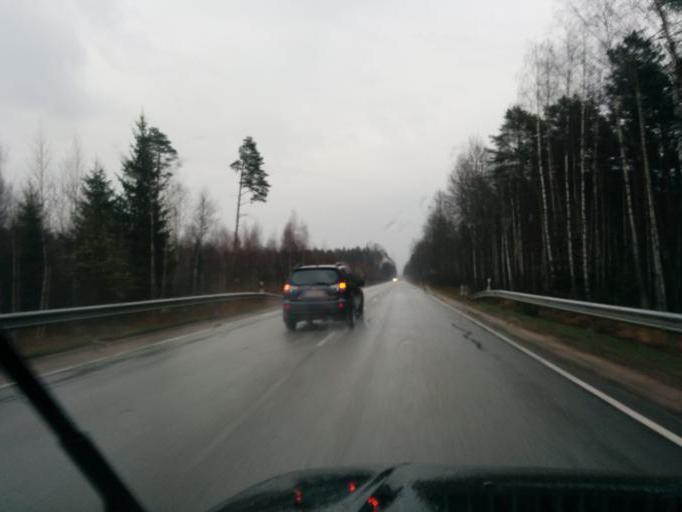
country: LV
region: Kekava
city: Balozi
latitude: 56.8183
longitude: 24.1111
